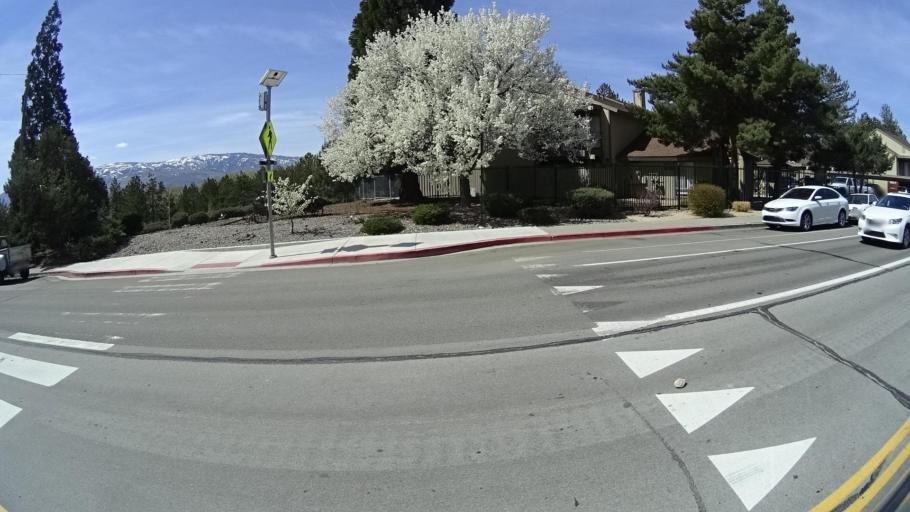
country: US
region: Nevada
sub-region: Washoe County
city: Reno
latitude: 39.5427
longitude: -119.8205
